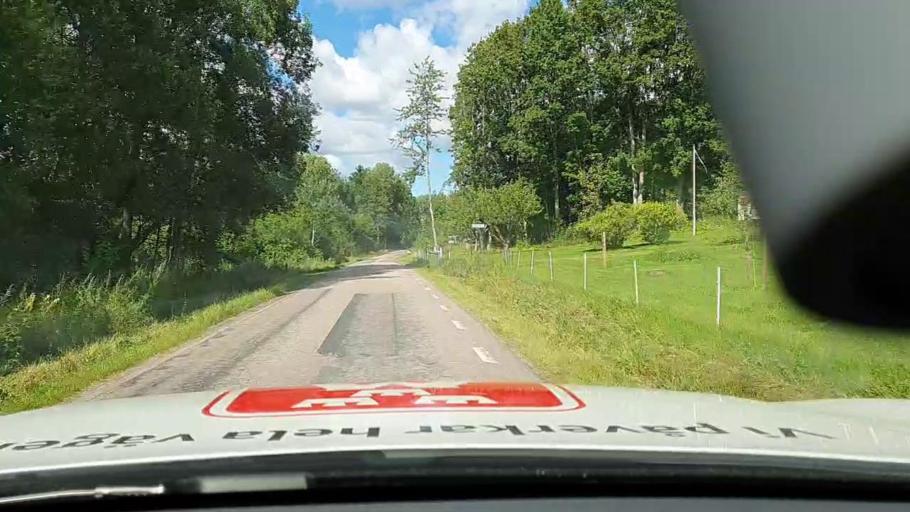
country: SE
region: Vaestra Goetaland
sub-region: Karlsborgs Kommun
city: Molltorp
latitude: 58.5949
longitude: 14.2640
